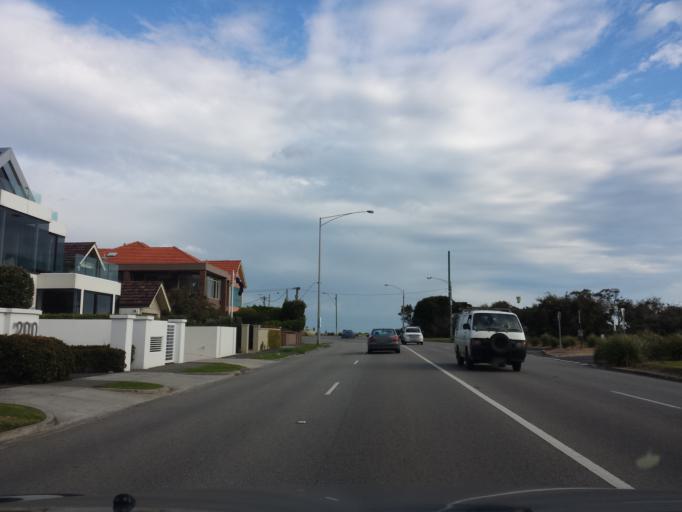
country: AU
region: Victoria
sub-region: Bayside
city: North Brighton
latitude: -37.9117
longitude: 144.9859
